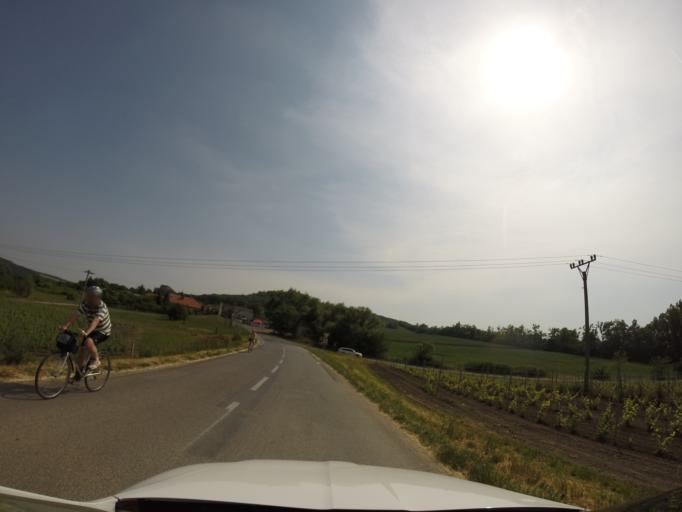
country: CZ
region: South Moravian
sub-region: Okres Breclav
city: Mikulov
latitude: 48.8525
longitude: 16.6429
